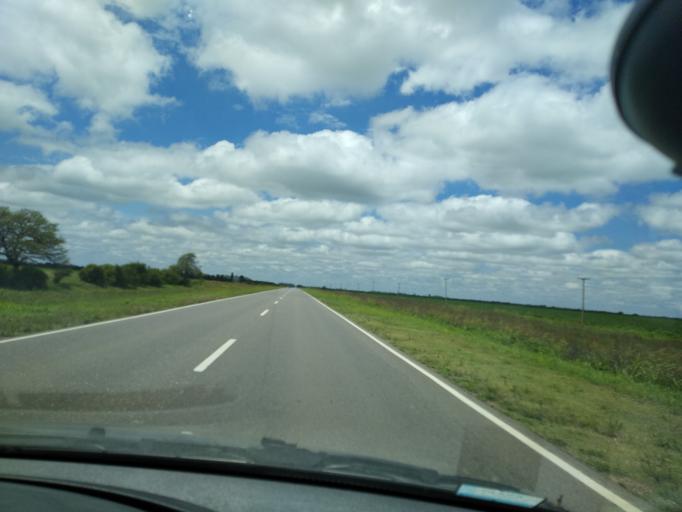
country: AR
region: Cordoba
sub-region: Departamento de Rio Segundo
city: Rio Segundo
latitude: -31.6439
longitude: -63.9786
